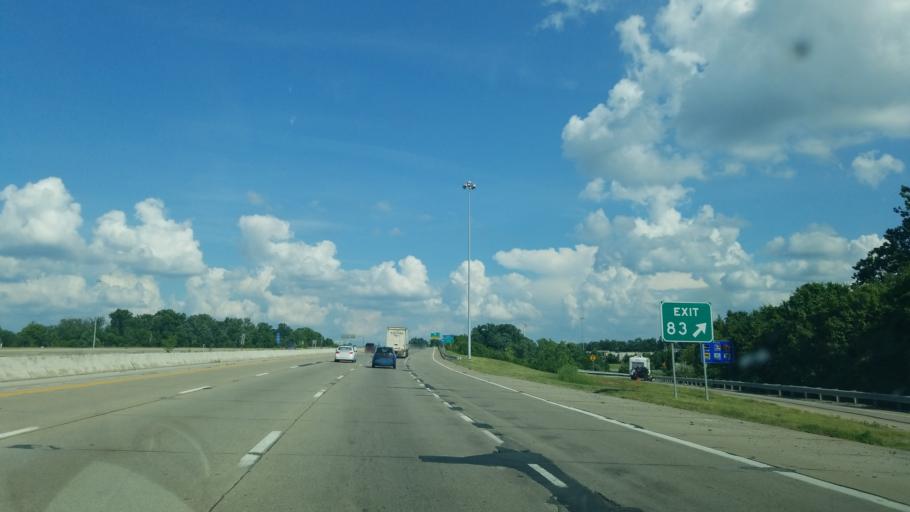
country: US
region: Kentucky
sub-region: Kenton County
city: Crestview Hills
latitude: 39.0304
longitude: -84.5814
